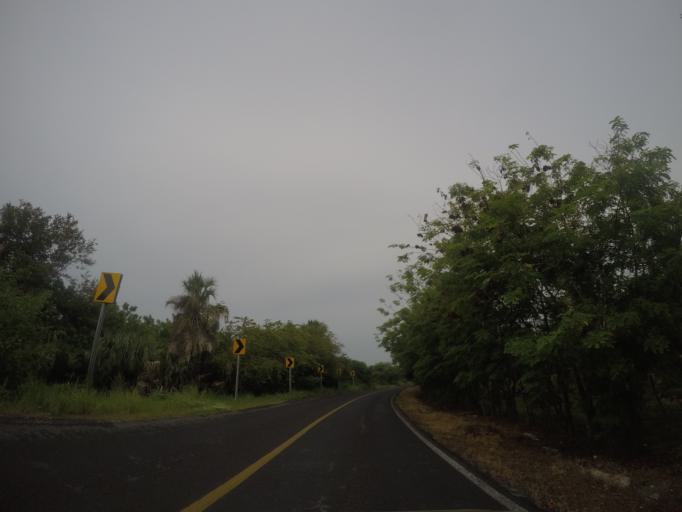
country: MX
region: Oaxaca
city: San Pedro Mixtepec
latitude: 15.9543
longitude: -97.2316
